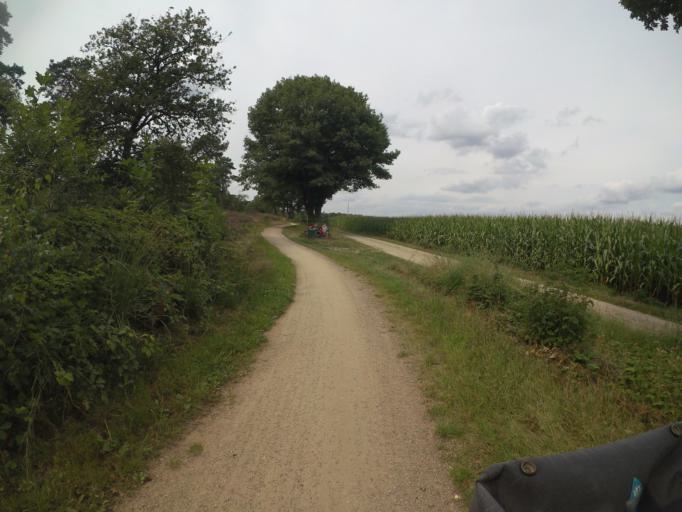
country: NL
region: Limburg
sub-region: Gemeente Bergen
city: Wellerlooi
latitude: 51.5518
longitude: 6.1493
